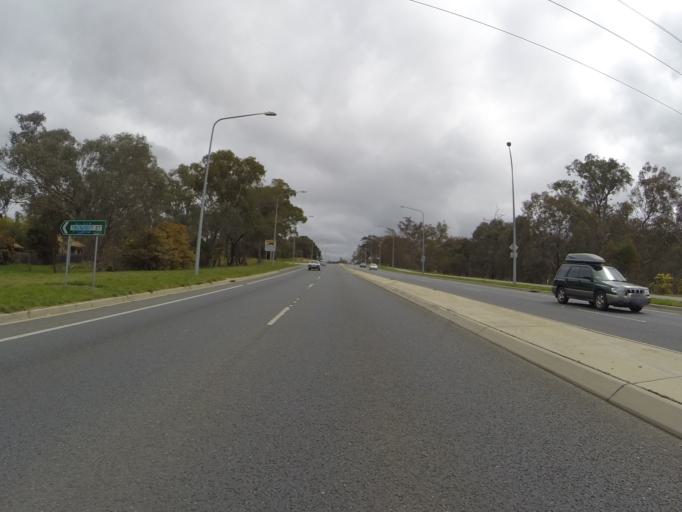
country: AU
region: Australian Capital Territory
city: Canberra
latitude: -35.2866
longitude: 149.1646
